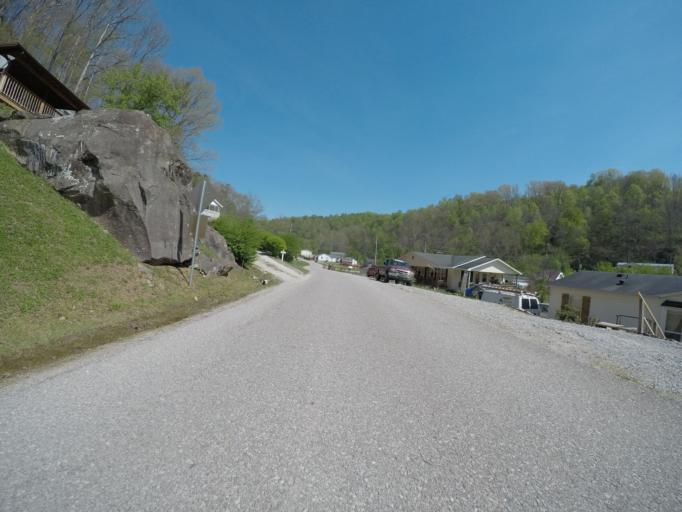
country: US
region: West Virginia
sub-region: Kanawha County
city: Charleston
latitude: 38.4138
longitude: -81.6111
